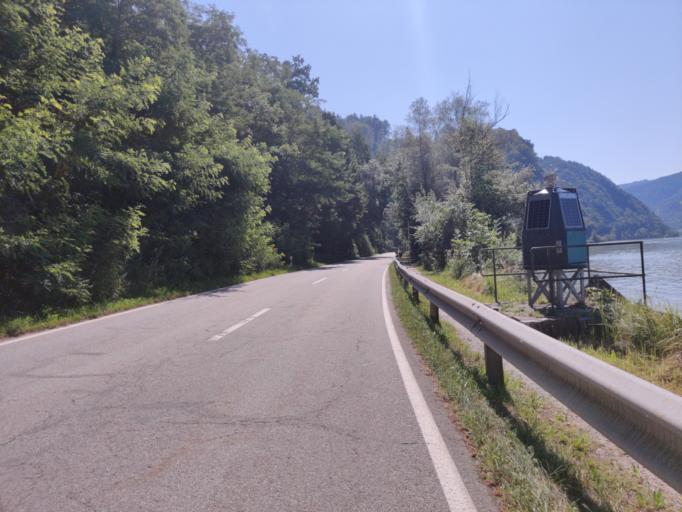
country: DE
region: Bavaria
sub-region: Lower Bavaria
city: Obernzell
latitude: 48.5514
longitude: 13.6529
